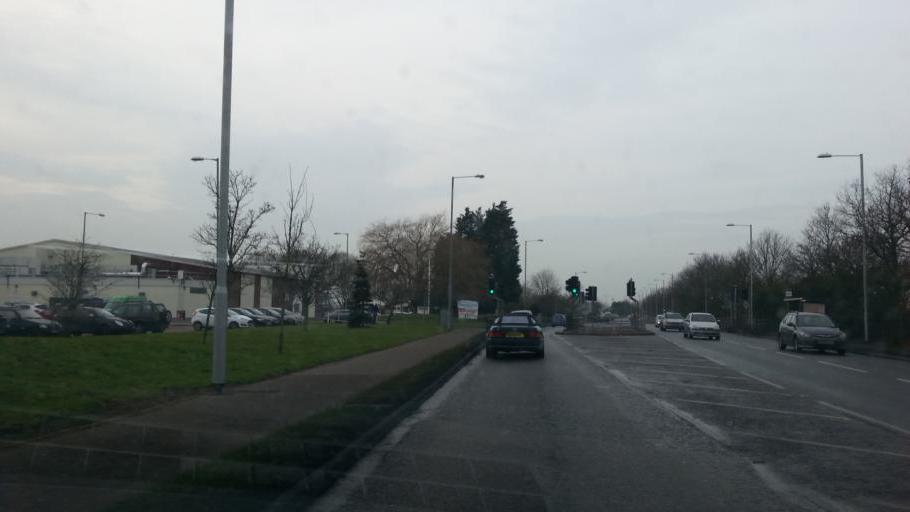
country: GB
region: England
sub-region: Essex
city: Canvey Island
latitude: 51.5343
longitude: 0.5696
